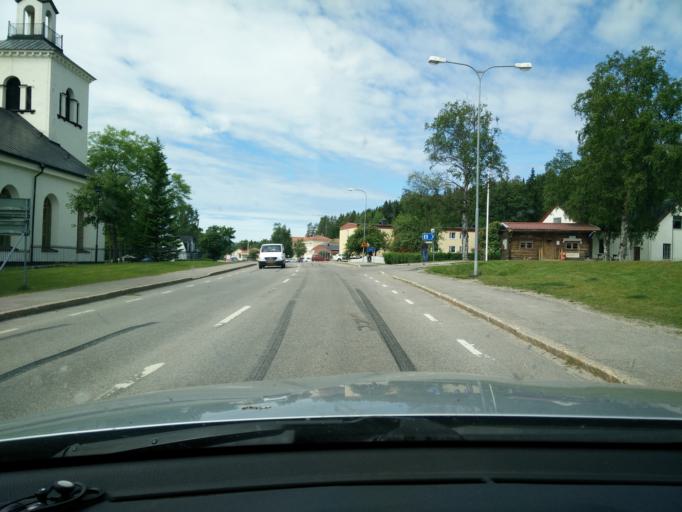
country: SE
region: Gaevleborg
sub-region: Hudiksvalls Kommun
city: Delsbo
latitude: 62.1099
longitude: 16.7098
